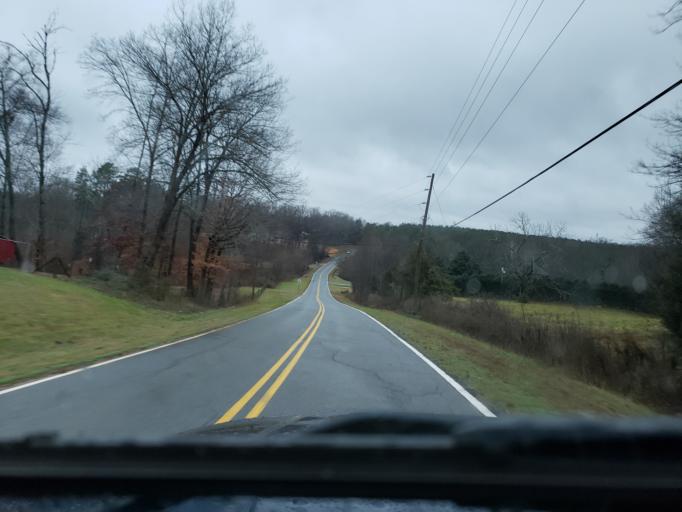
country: US
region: North Carolina
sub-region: Cleveland County
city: White Plains
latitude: 35.1811
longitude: -81.3715
